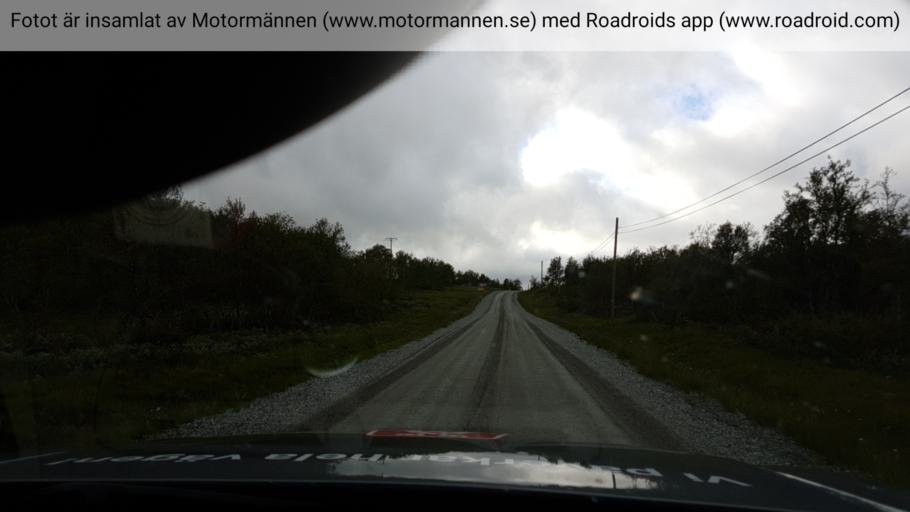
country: SE
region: Jaemtland
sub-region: Are Kommun
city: Are
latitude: 62.8936
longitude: 12.7127
